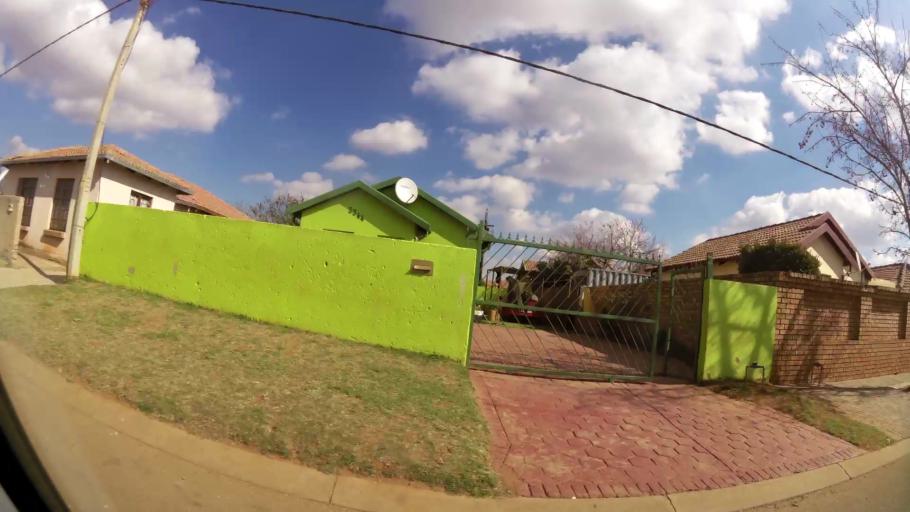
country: ZA
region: Gauteng
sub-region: City of Tshwane Metropolitan Municipality
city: Cullinan
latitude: -25.7055
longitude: 28.4160
